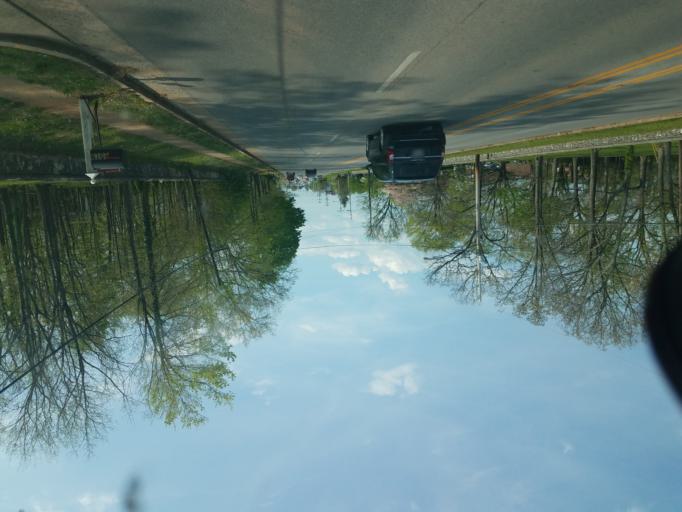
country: US
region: Kentucky
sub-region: Warren County
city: Bowling Green
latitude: 36.9737
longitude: -86.4360
